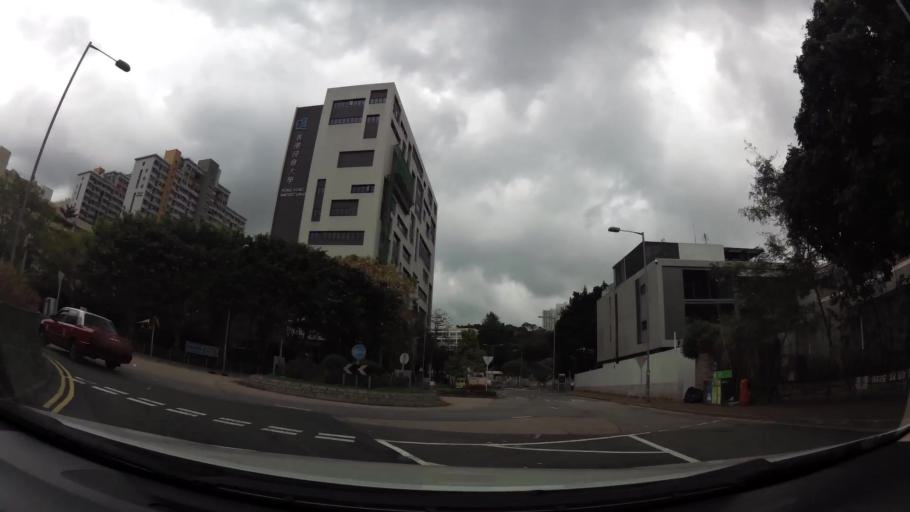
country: HK
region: Wong Tai Sin
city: Wong Tai Sin
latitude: 22.3340
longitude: 114.1813
